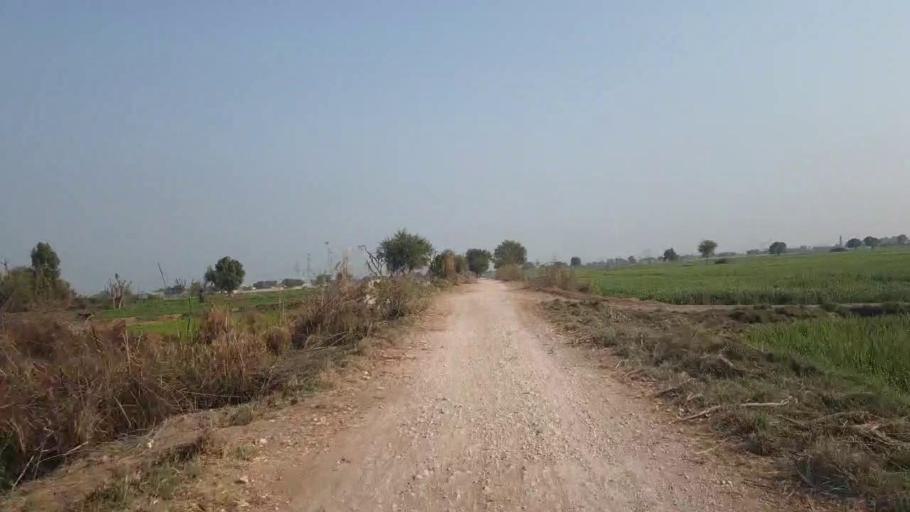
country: PK
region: Sindh
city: Hala
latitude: 25.8836
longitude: 68.4529
